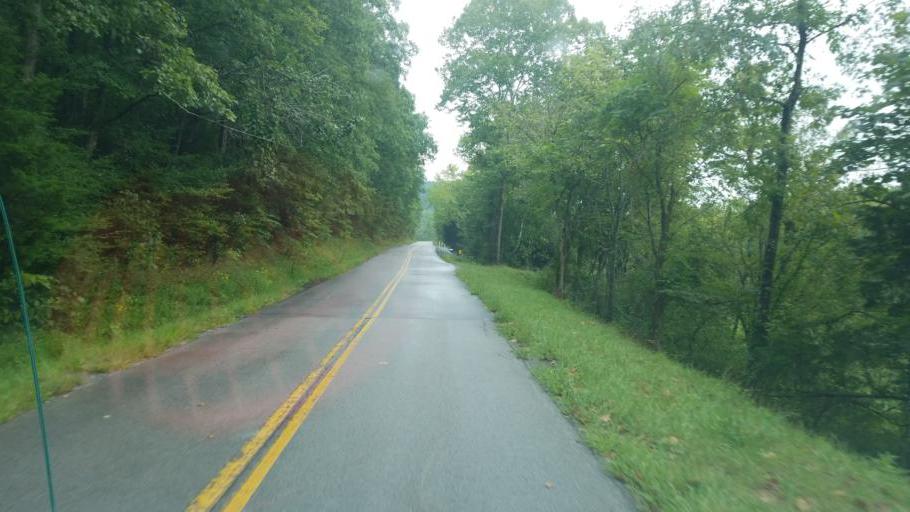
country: US
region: Kentucky
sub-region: Fleming County
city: Flemingsburg
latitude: 38.3884
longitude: -83.5490
